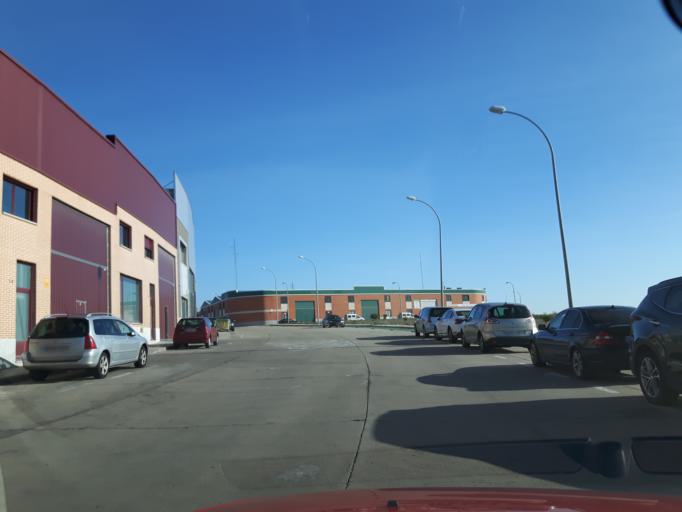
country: ES
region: Castille and Leon
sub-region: Provincia de Salamanca
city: Villares de la Reina
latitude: 40.9922
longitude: -5.6506
